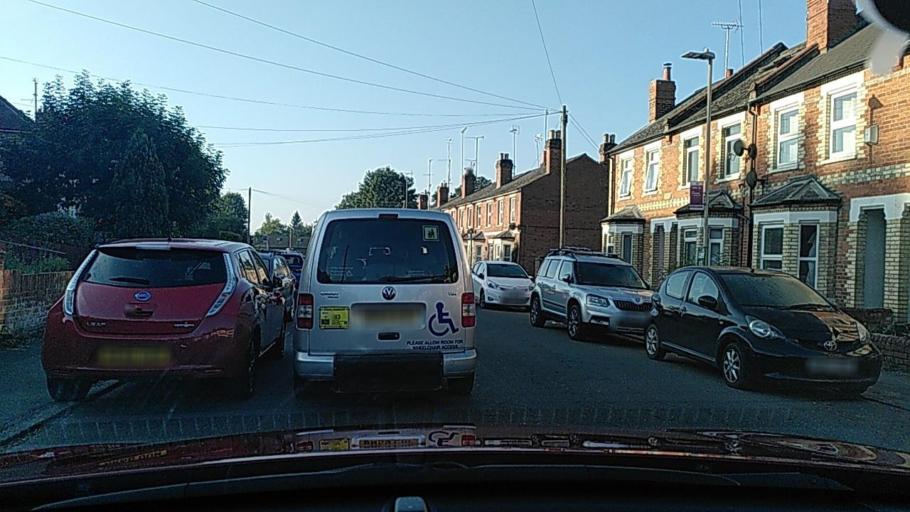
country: GB
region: England
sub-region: Reading
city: Reading
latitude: 51.4728
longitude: -0.9748
